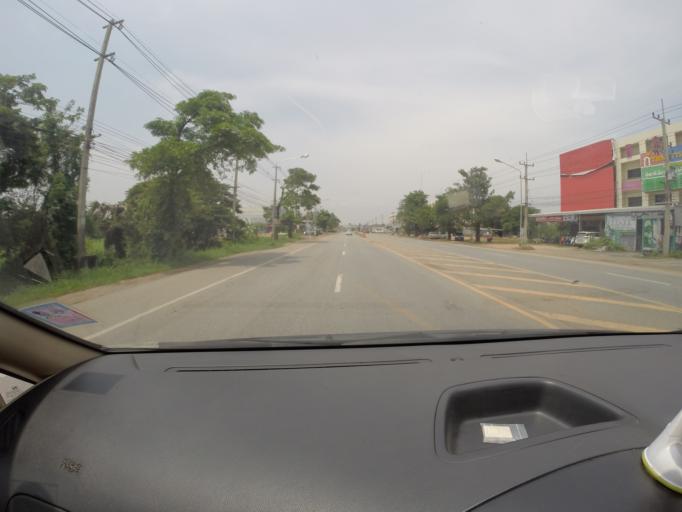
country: TH
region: Chaiyaphum
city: Chaiyaphum
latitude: 15.6887
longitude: 102.0110
